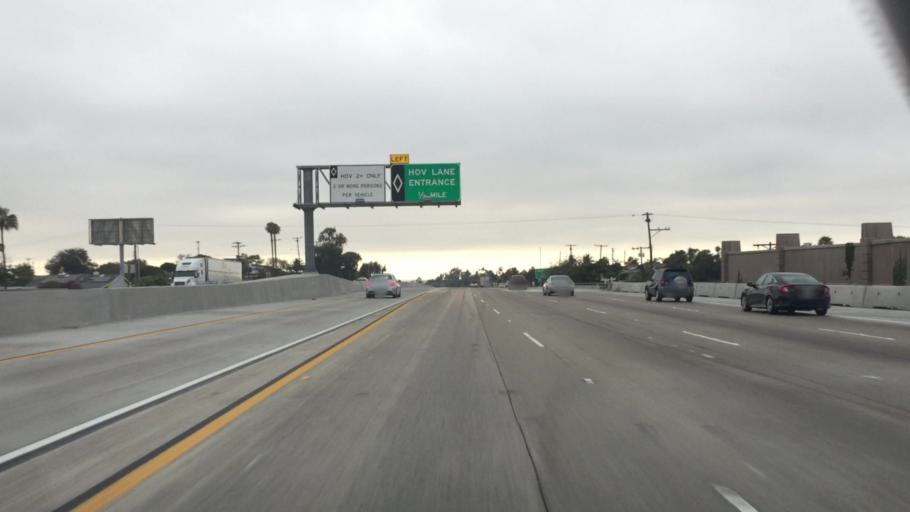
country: US
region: California
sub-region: San Diego County
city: Bonita
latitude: 32.6208
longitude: -117.0402
